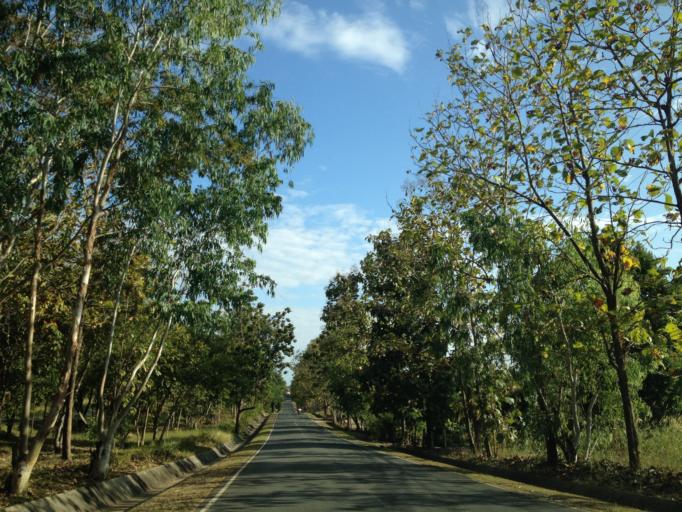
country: TH
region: Chiang Mai
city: Chiang Mai
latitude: 18.8610
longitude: 98.9493
